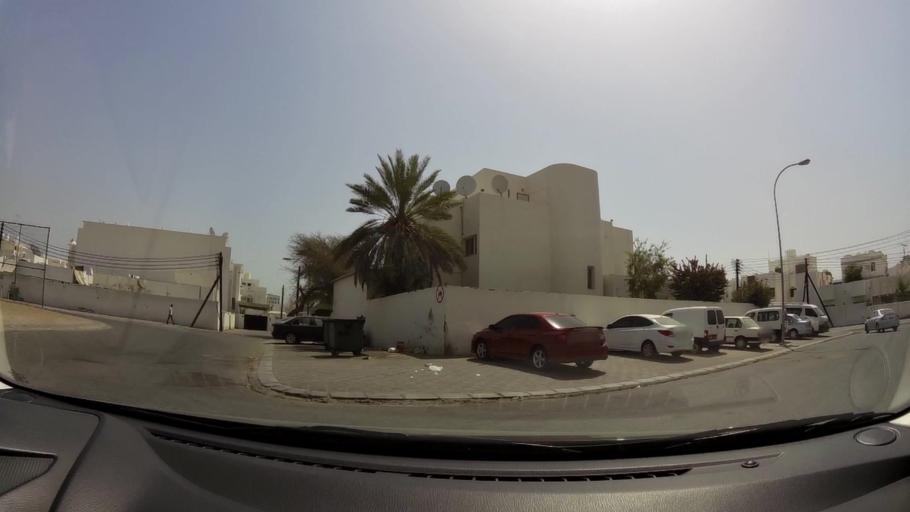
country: OM
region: Muhafazat Masqat
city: Bawshar
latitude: 23.5895
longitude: 58.4240
